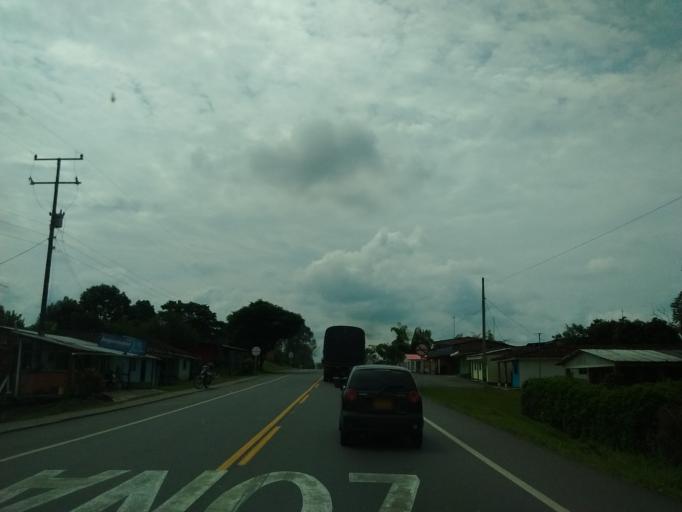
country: CO
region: Cauca
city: Morales
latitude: 2.7578
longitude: -76.5542
